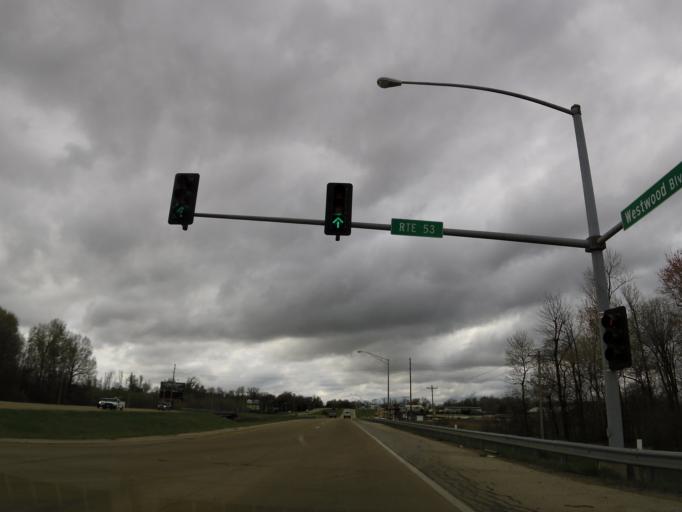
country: US
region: Missouri
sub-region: Butler County
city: Poplar Bluff
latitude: 36.7445
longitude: -90.4135
